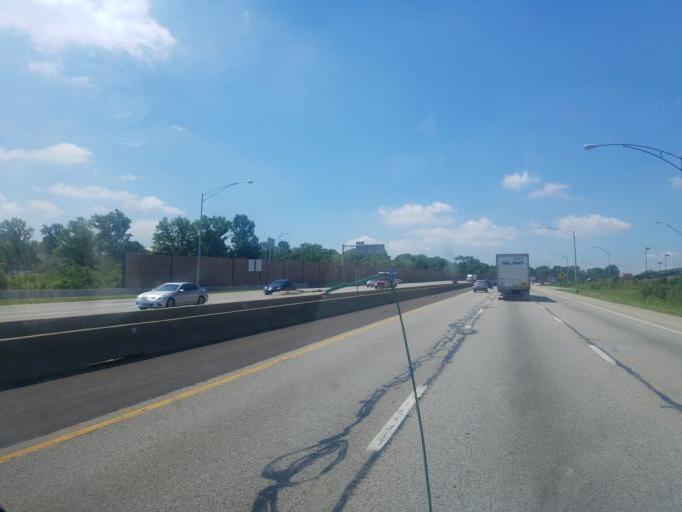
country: US
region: Ohio
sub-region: Hamilton County
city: Kenwood
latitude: 39.2003
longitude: -84.3747
